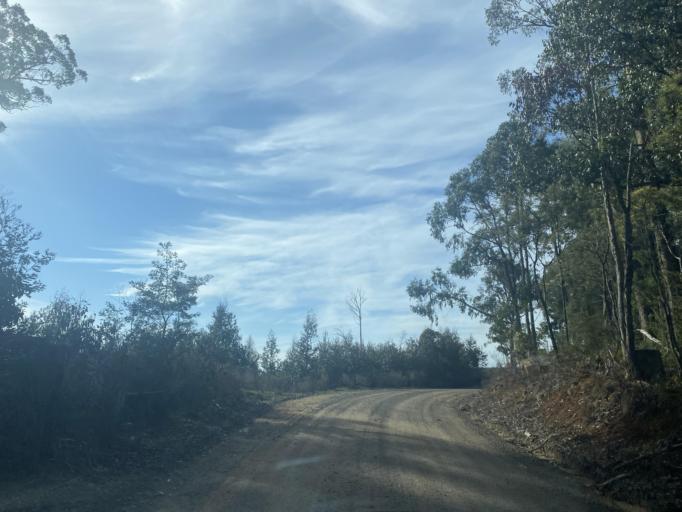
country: AU
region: Victoria
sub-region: Mansfield
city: Mansfield
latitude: -36.8515
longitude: 146.1804
